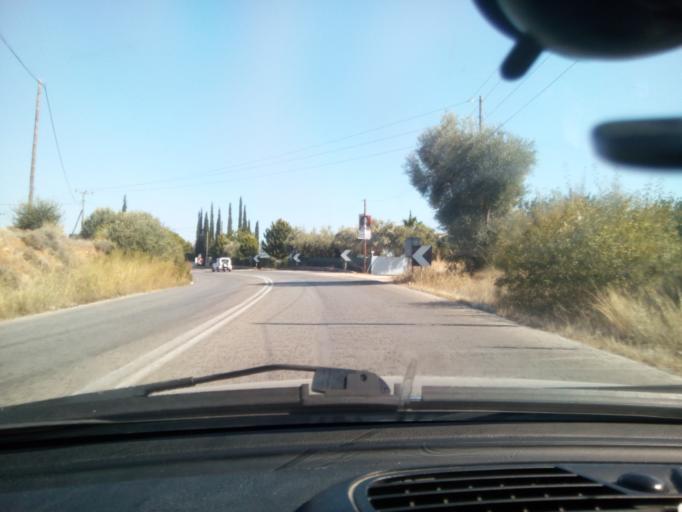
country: GR
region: Central Greece
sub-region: Nomos Evvoias
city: Filla
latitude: 38.4113
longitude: 23.7164
